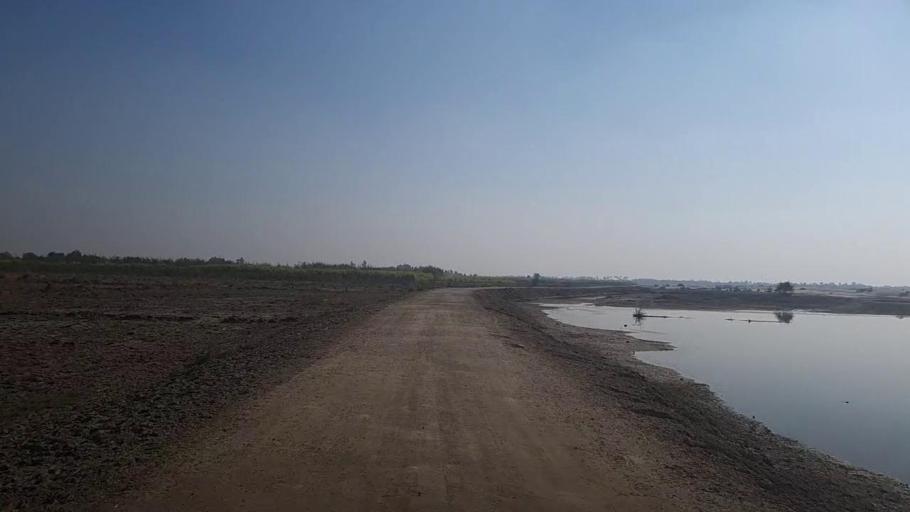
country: PK
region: Sindh
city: Khairpur
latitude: 27.4398
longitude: 68.7276
